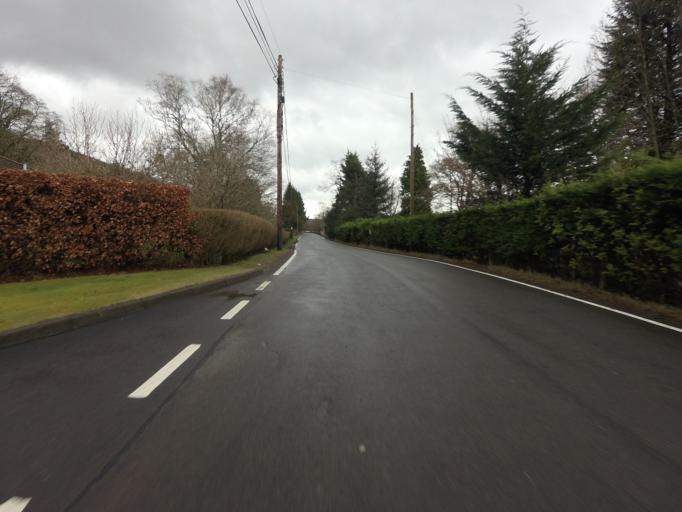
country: GB
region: Scotland
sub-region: Stirling
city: Killearn
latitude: 56.1878
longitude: -4.4795
